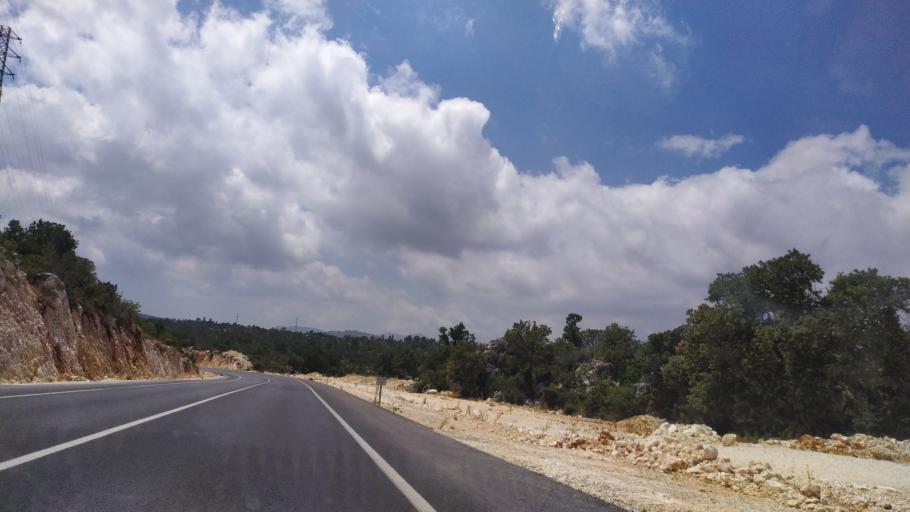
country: TR
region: Mersin
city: Gulnar
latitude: 36.2655
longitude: 33.3672
